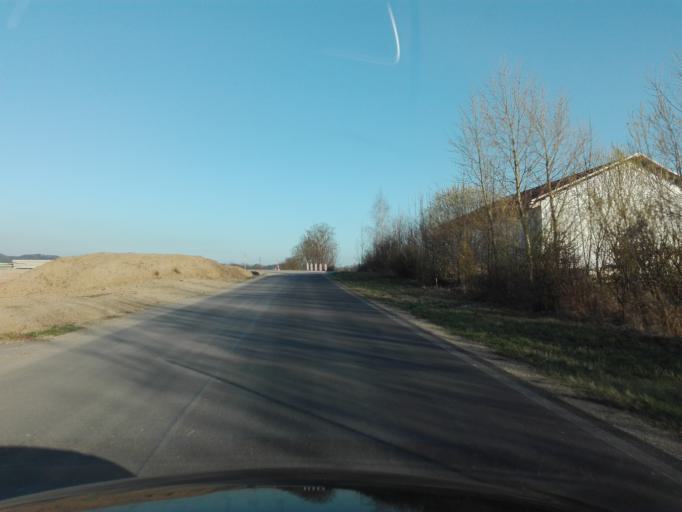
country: AT
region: Upper Austria
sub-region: Politischer Bezirk Perg
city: Perg
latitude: 48.2215
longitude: 14.6988
